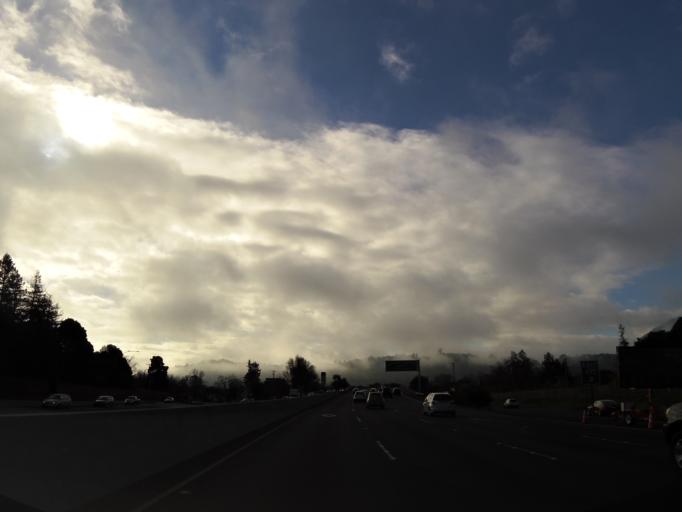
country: US
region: California
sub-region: Marin County
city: San Rafael
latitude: 37.9760
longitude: -122.5207
